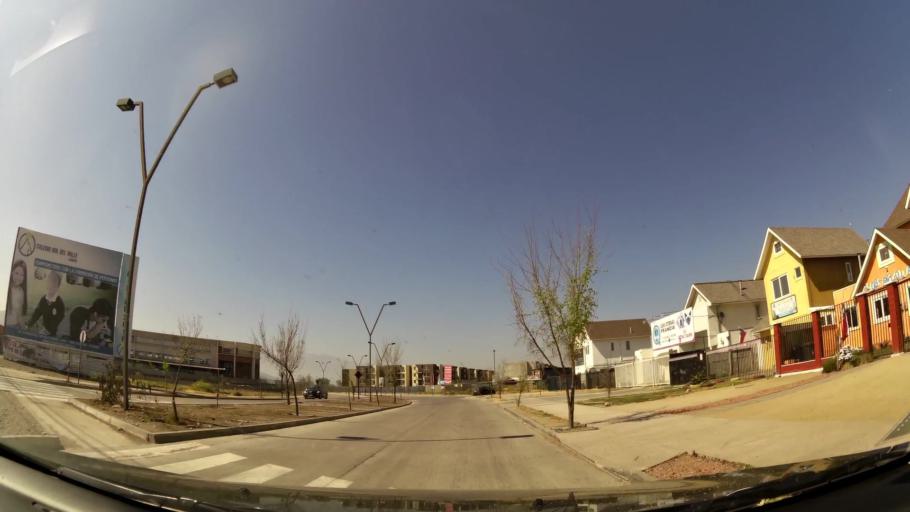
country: CL
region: Santiago Metropolitan
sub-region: Provincia de Chacabuco
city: Chicureo Abajo
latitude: -33.3249
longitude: -70.7429
